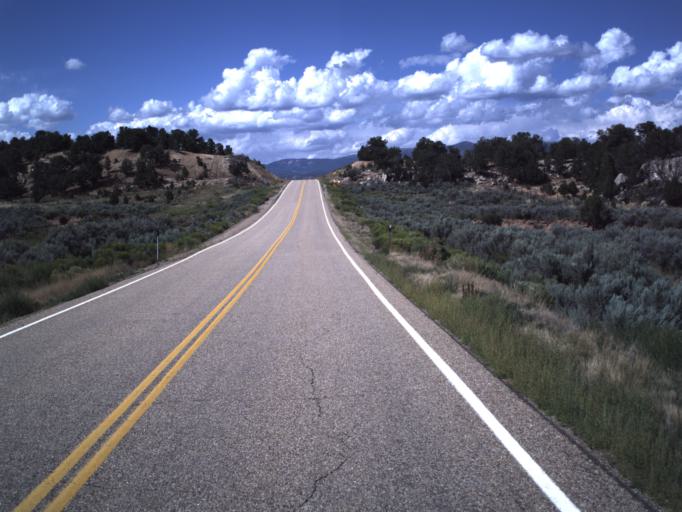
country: US
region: Utah
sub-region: Duchesne County
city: Duchesne
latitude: 40.2910
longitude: -110.6951
